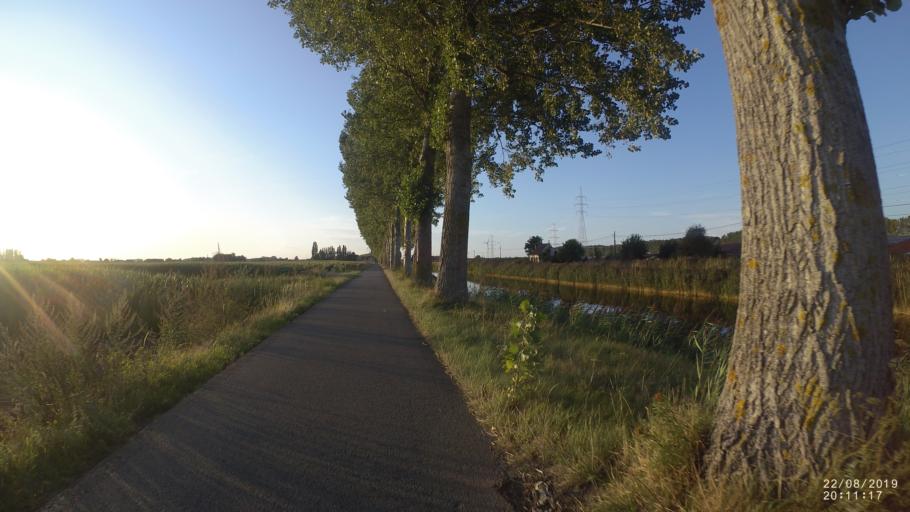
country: BE
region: Flanders
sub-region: Provincie Oost-Vlaanderen
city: Eeklo
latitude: 51.1640
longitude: 3.5436
